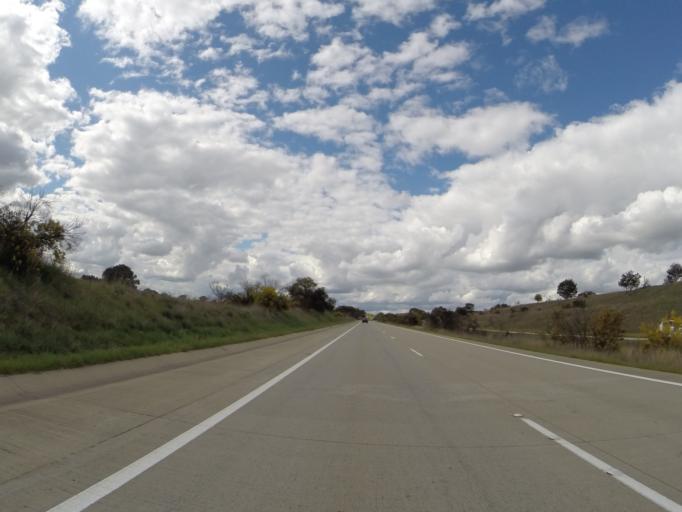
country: AU
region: New South Wales
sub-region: Yass Valley
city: Murrumbateman
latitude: -34.8063
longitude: 149.1319
